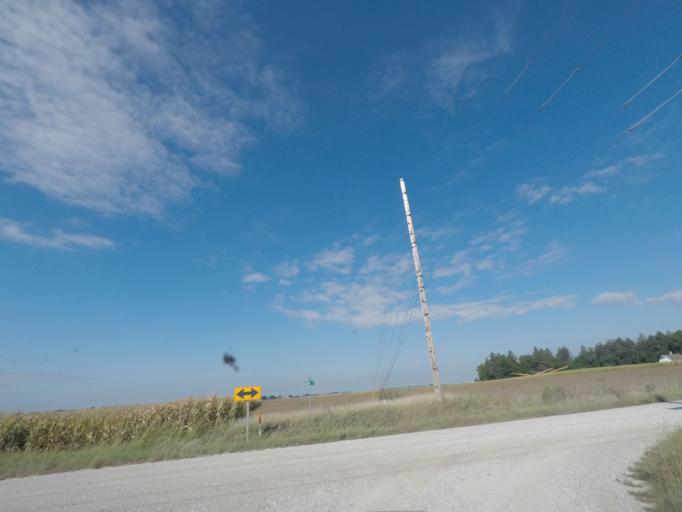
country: US
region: Iowa
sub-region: Story County
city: Nevada
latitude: 42.0345
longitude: -93.4251
